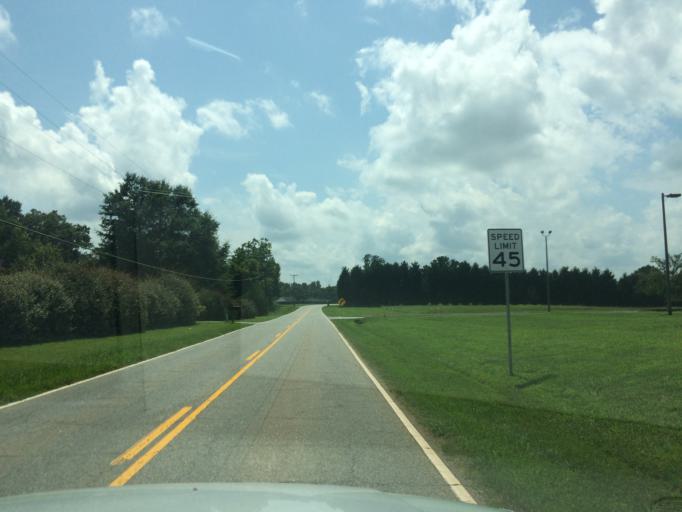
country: US
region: South Carolina
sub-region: Greenville County
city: Five Forks
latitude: 34.8401
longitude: -82.1677
